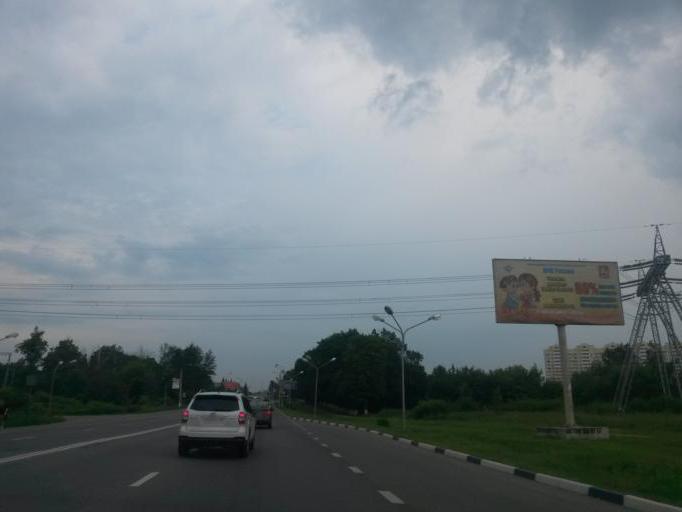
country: RU
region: Moskovskaya
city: Domodedovo
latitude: 55.4583
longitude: 37.7589
